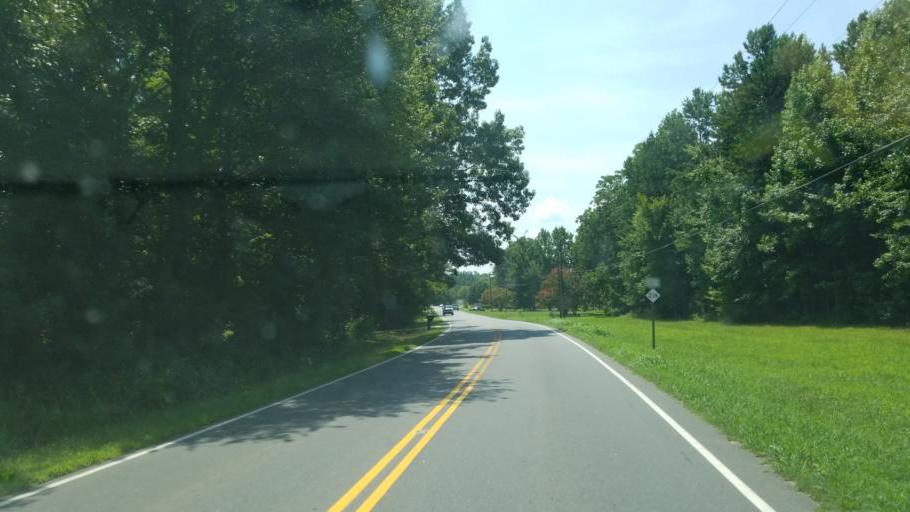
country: US
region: North Carolina
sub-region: Gaston County
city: Tryon
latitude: 35.3483
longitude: -81.3499
